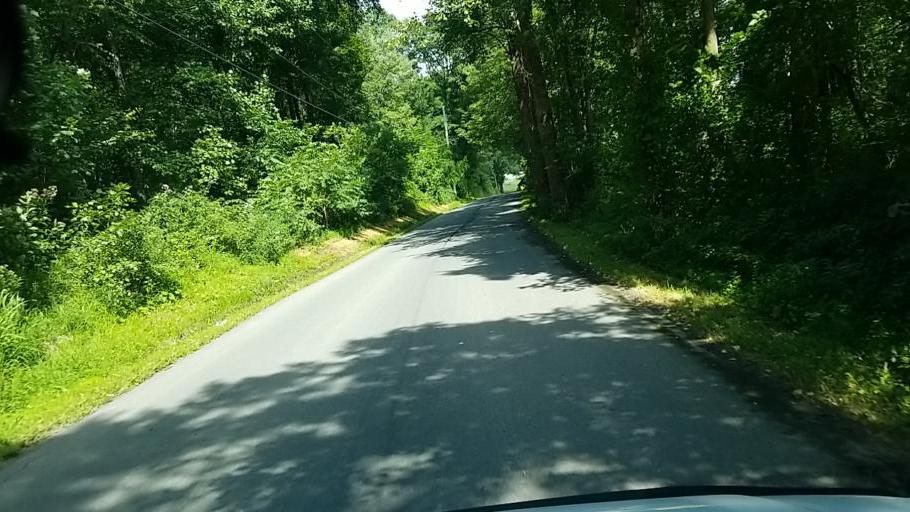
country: US
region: Pennsylvania
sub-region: Dauphin County
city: Elizabethville
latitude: 40.6118
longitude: -76.8495
